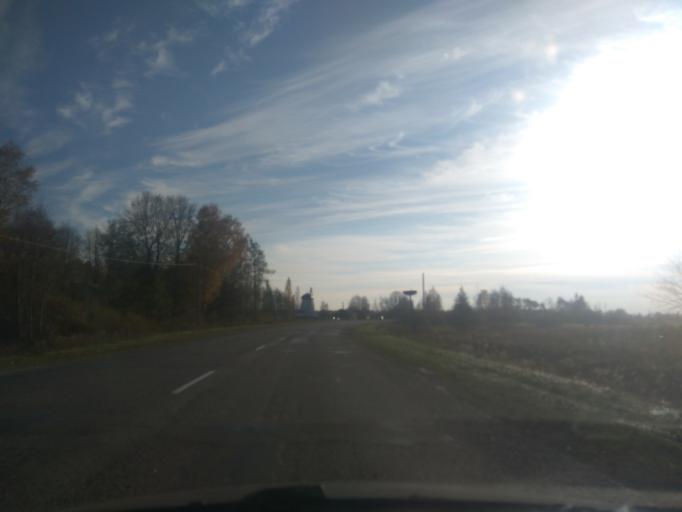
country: LV
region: Ventspils
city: Ventspils
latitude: 57.3438
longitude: 21.5693
